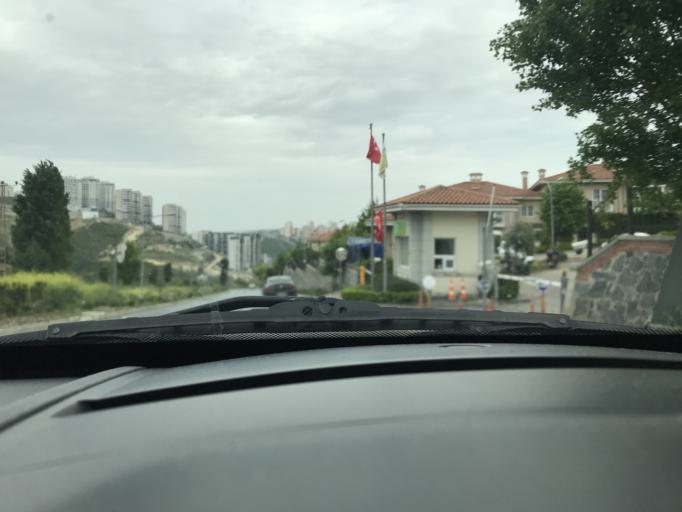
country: TR
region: Istanbul
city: Esenyurt
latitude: 41.0901
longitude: 28.6819
